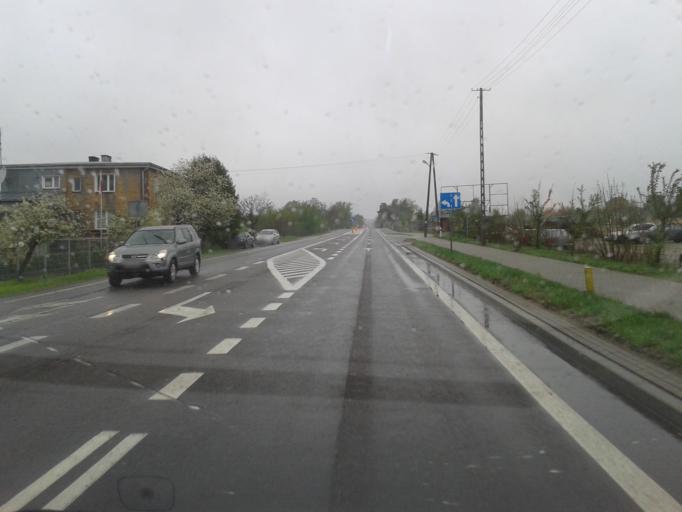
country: PL
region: Lublin Voivodeship
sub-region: Powiat tomaszowski
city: Belzec
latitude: 50.3725
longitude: 23.4551
